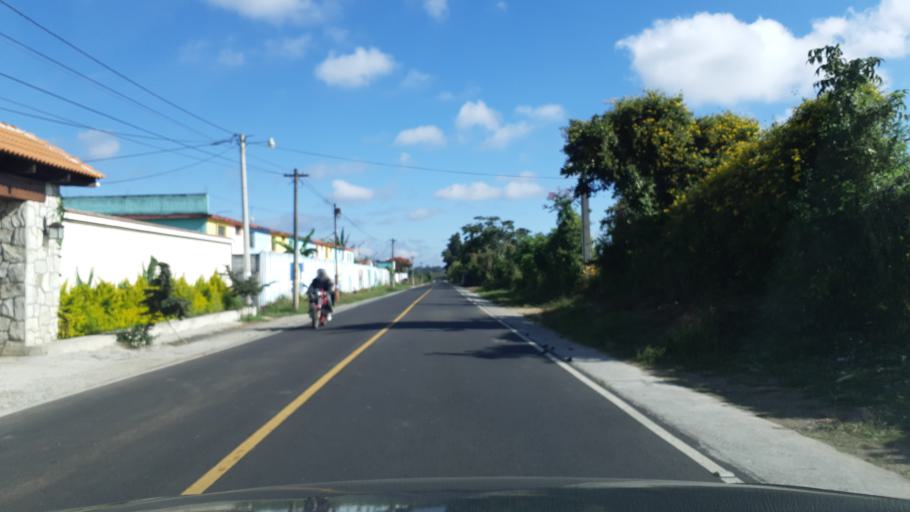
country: GT
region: Chimaltenango
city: San Andres Itzapa
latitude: 14.6330
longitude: -90.8285
